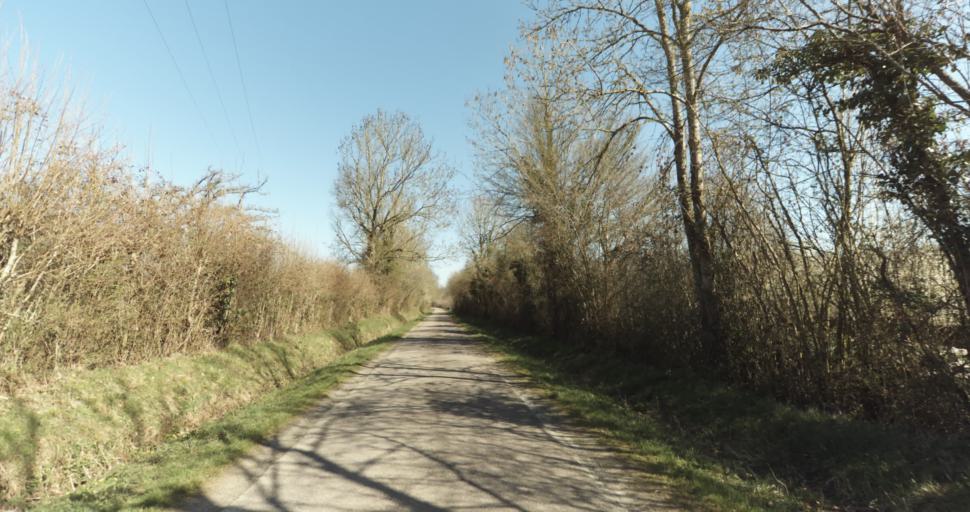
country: FR
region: Lower Normandy
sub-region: Departement du Calvados
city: Livarot
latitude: 49.0000
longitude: 0.0701
